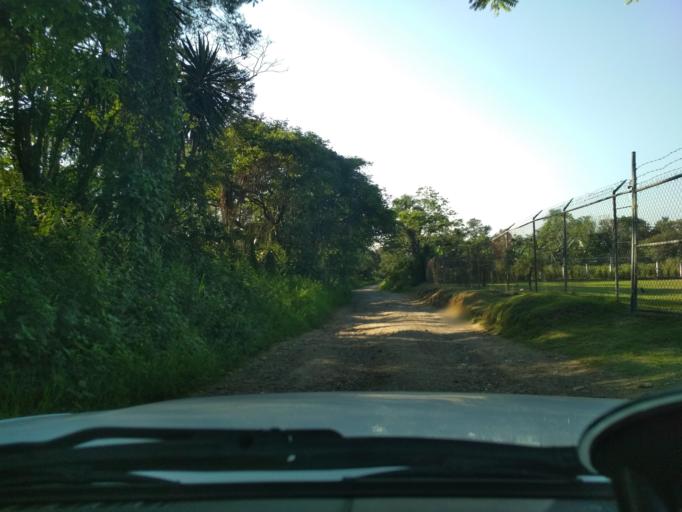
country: MX
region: Veracruz
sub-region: Fortin
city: Fraccionamiento Villas de la Llave
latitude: 18.9203
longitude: -96.9894
